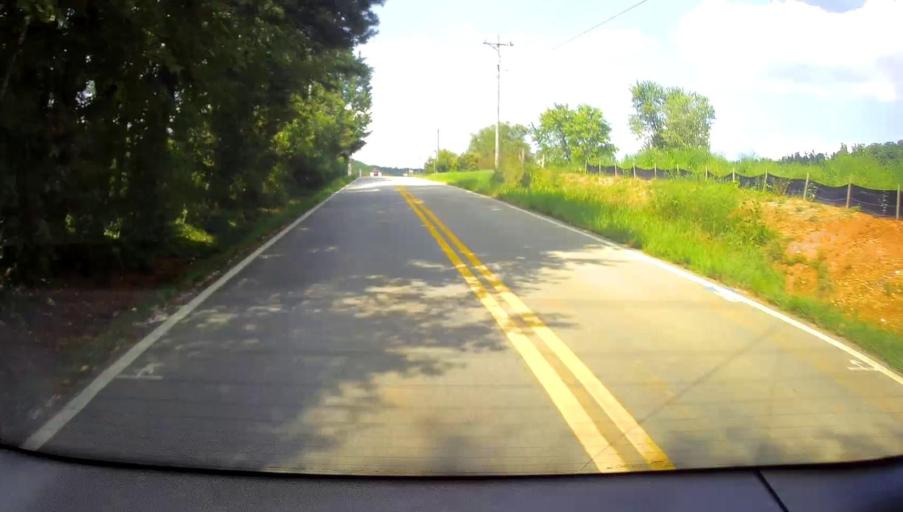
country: US
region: Georgia
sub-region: Catoosa County
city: Ringgold
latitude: 34.9389
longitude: -85.0826
